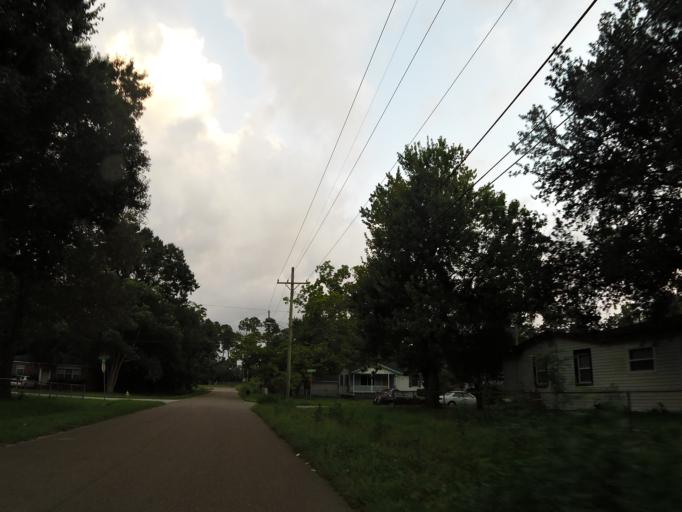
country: US
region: Florida
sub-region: Duval County
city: Jacksonville
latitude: 30.3299
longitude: -81.7268
